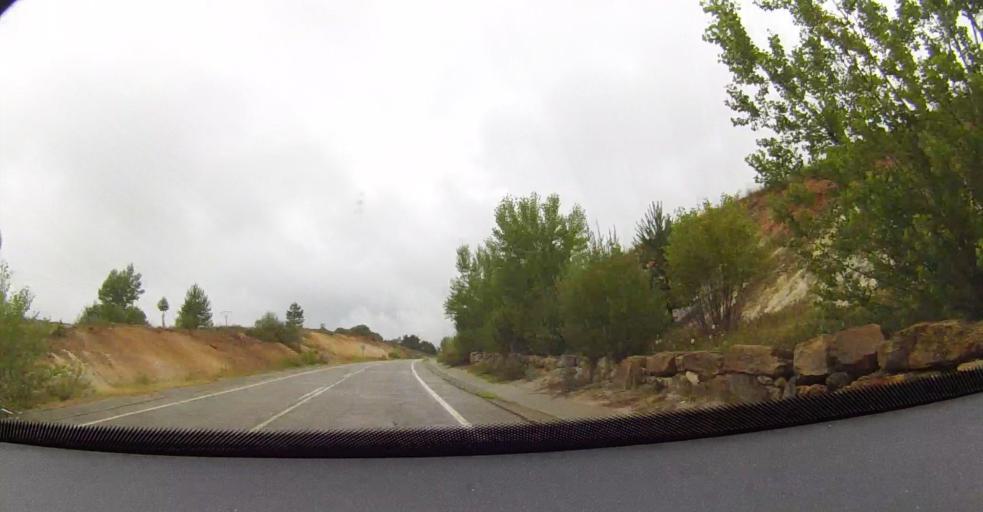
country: ES
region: Castille and Leon
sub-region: Provincia de Leon
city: Bonar
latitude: 42.8465
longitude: -5.2689
